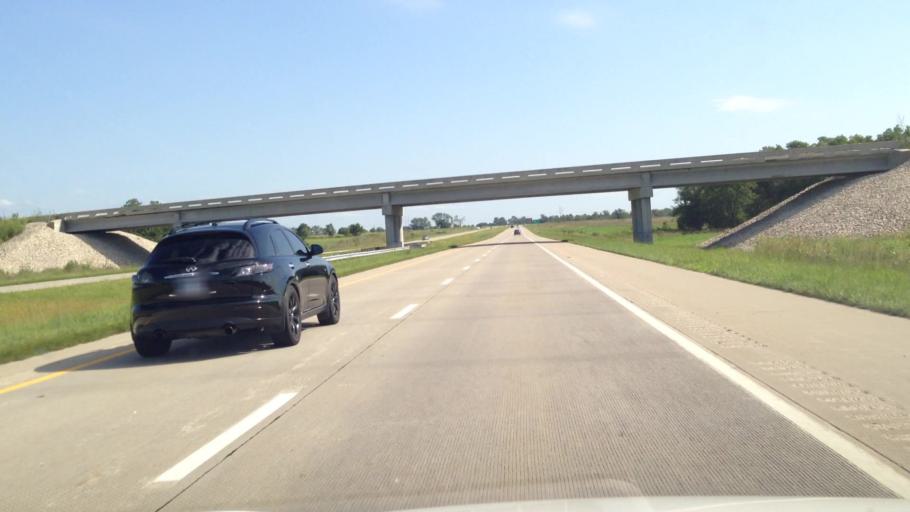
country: US
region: Kansas
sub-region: Linn County
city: La Cygne
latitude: 38.2878
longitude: -94.6743
